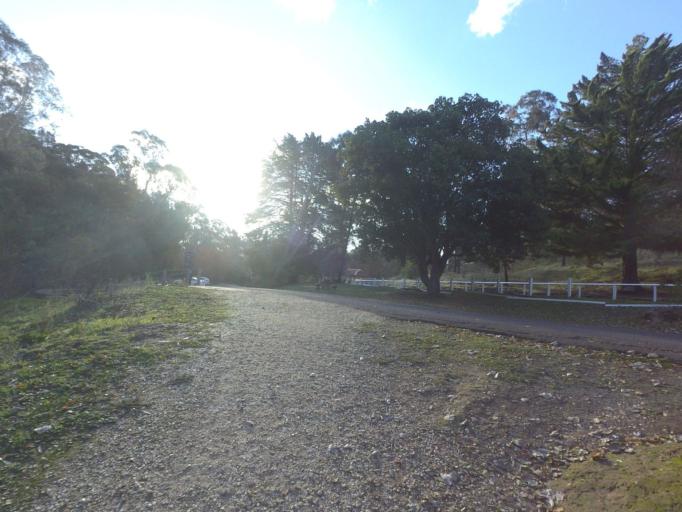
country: AU
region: Victoria
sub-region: Mount Alexander
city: Castlemaine
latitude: -37.1618
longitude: 144.2146
